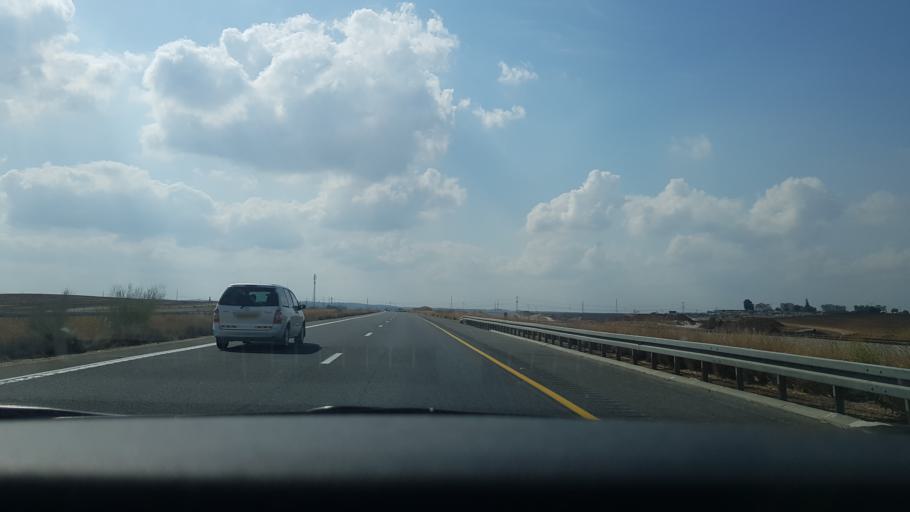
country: IL
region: Central District
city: Bene 'Ayish
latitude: 31.7272
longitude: 34.8209
